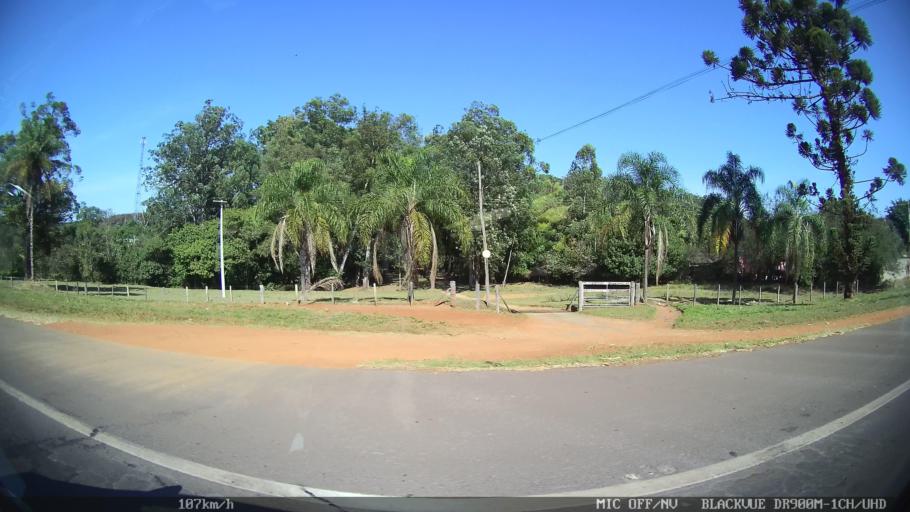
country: BR
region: Sao Paulo
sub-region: Batatais
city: Batatais
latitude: -20.9089
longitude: -47.5941
